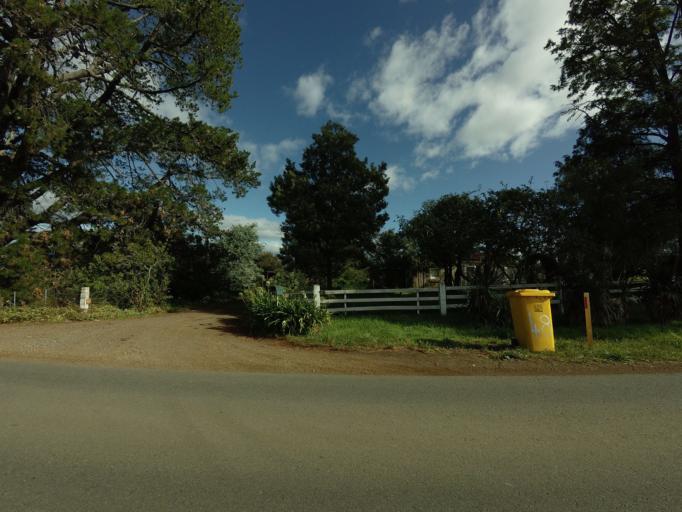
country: AU
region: Tasmania
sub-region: Derwent Valley
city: New Norfolk
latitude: -42.6941
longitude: 146.9341
